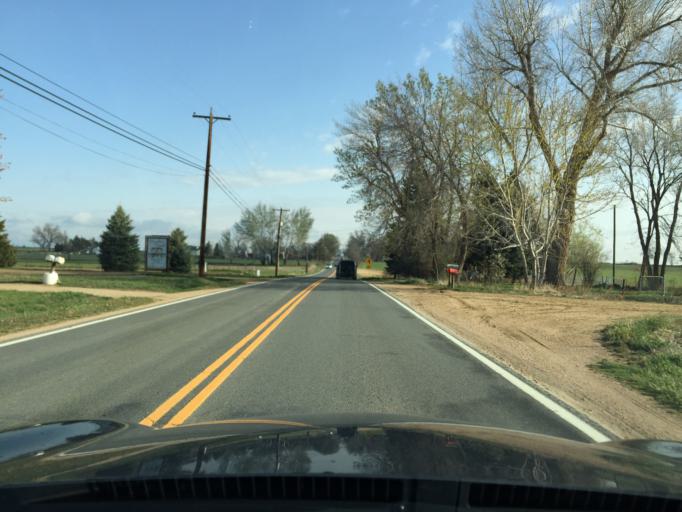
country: US
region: Colorado
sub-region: Boulder County
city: Erie
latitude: 40.1125
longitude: -105.0554
